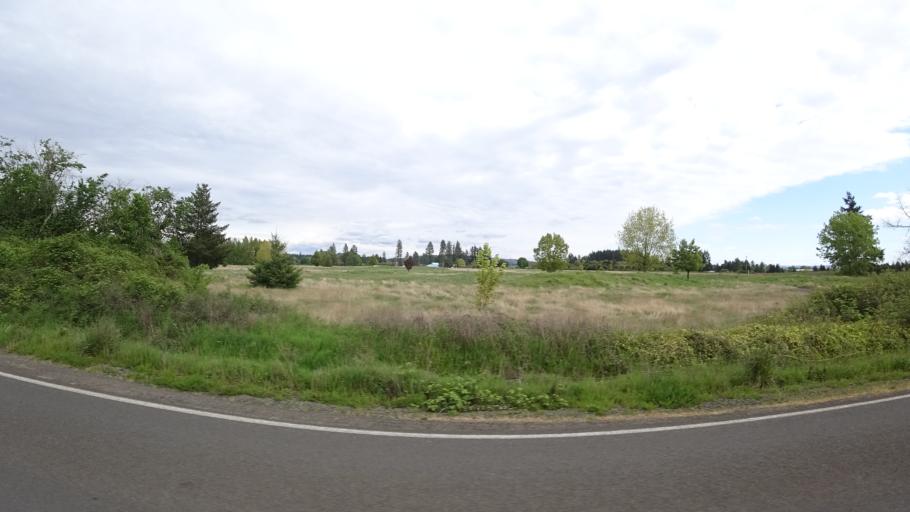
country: US
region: Oregon
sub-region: Washington County
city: Hillsboro
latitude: 45.4765
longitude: -122.9539
